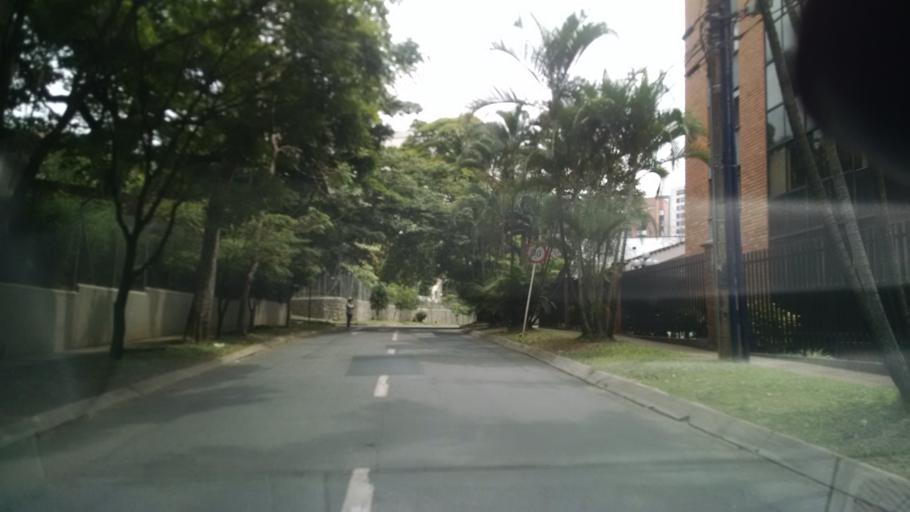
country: CO
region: Antioquia
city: Itagui
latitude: 6.2075
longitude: -75.5729
